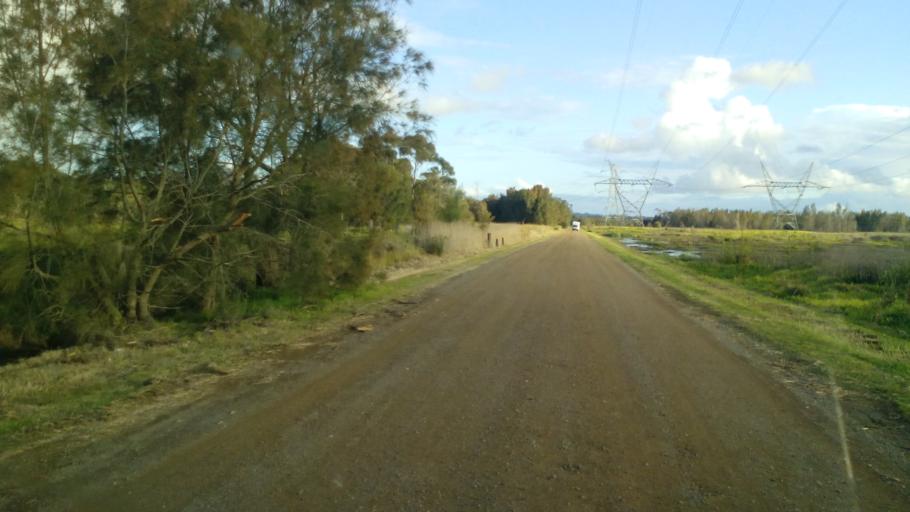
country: AU
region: New South Wales
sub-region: Newcastle
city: Mayfield West
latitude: -32.8345
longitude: 151.7088
